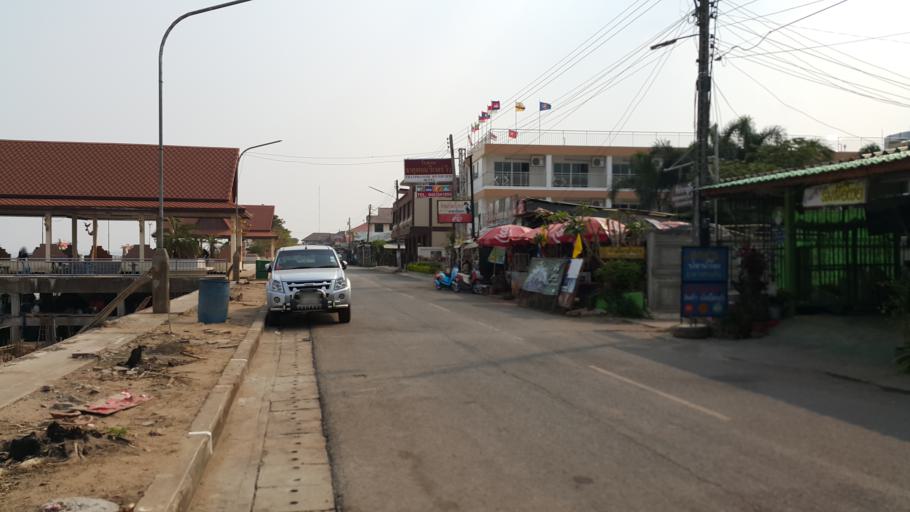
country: TH
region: Nakhon Phanom
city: That Phanom
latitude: 16.9459
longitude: 104.7297
